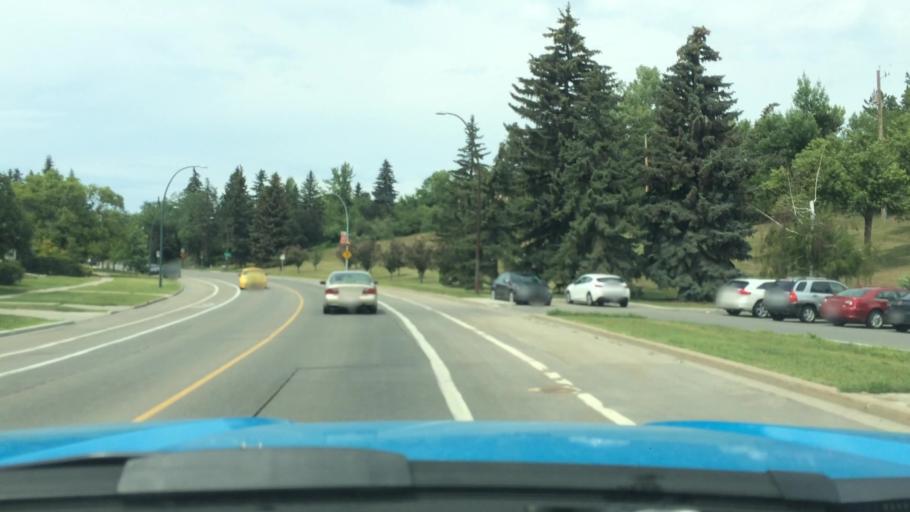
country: CA
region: Alberta
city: Calgary
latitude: 51.0776
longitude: -114.0847
